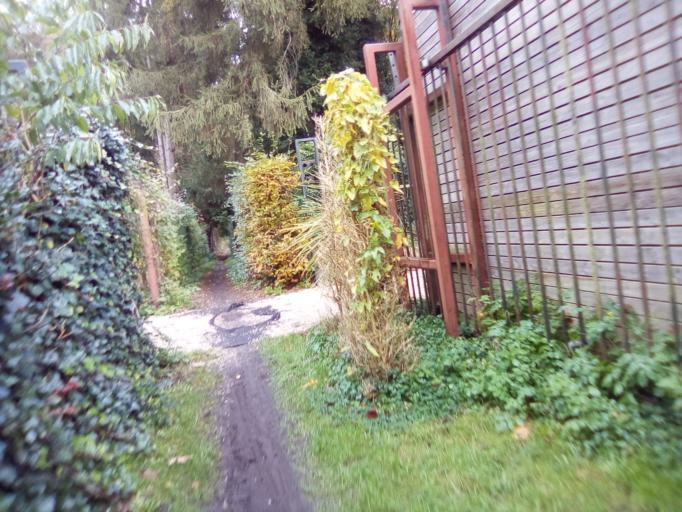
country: BE
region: Flanders
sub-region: Provincie Oost-Vlaanderen
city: Lokeren
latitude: 51.1174
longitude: 3.9975
